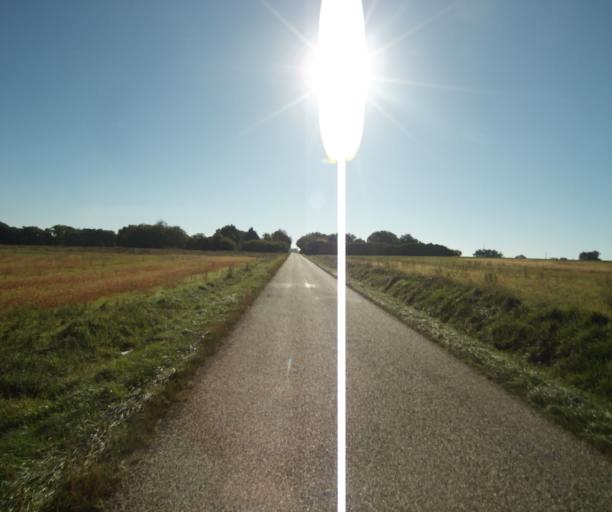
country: FR
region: Midi-Pyrenees
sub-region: Departement du Gers
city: Gondrin
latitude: 43.8265
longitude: 0.2670
